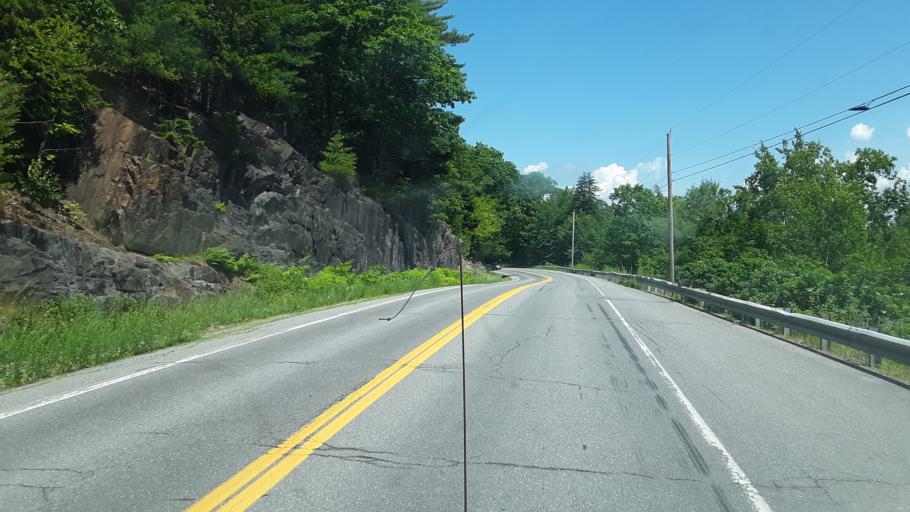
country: US
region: Maine
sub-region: Hancock County
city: Bucksport
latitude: 44.5623
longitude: -68.8046
